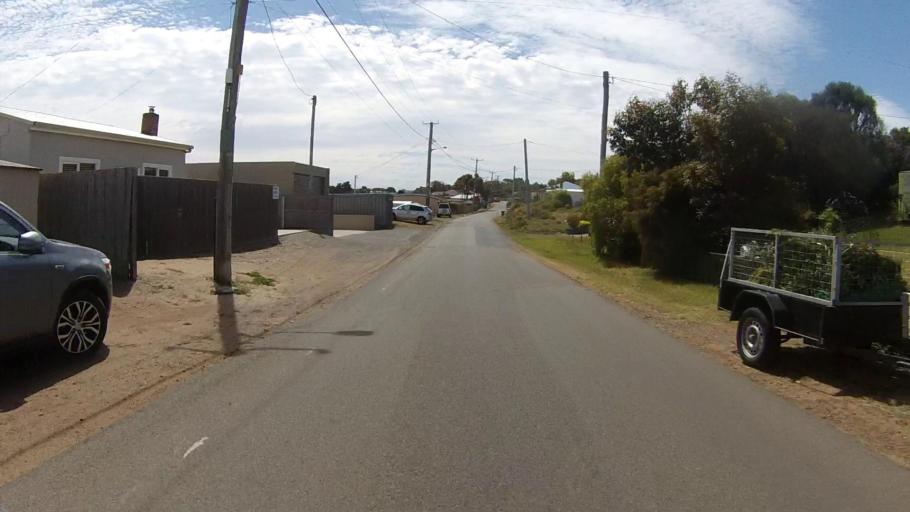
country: AU
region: Tasmania
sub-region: Kingborough
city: Taroona
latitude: -42.9920
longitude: 147.4041
